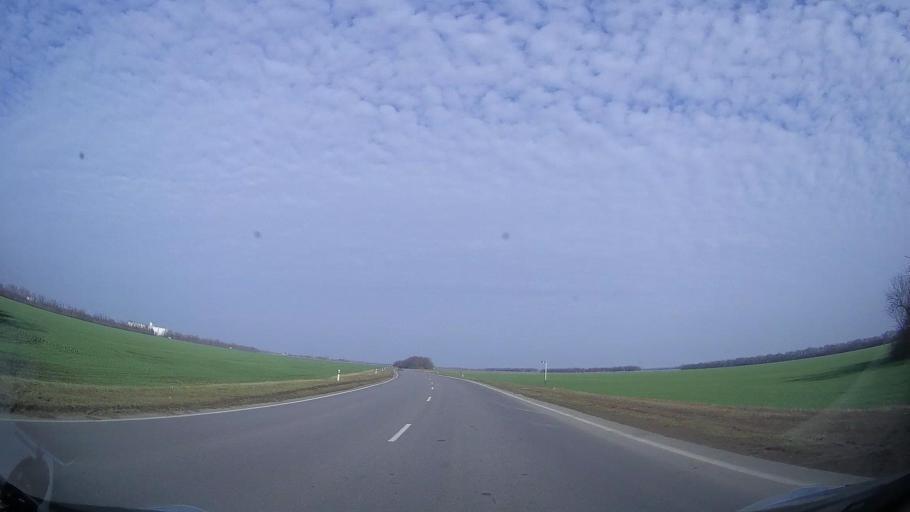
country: RU
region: Rostov
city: Tselina
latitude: 46.5171
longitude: 41.0723
